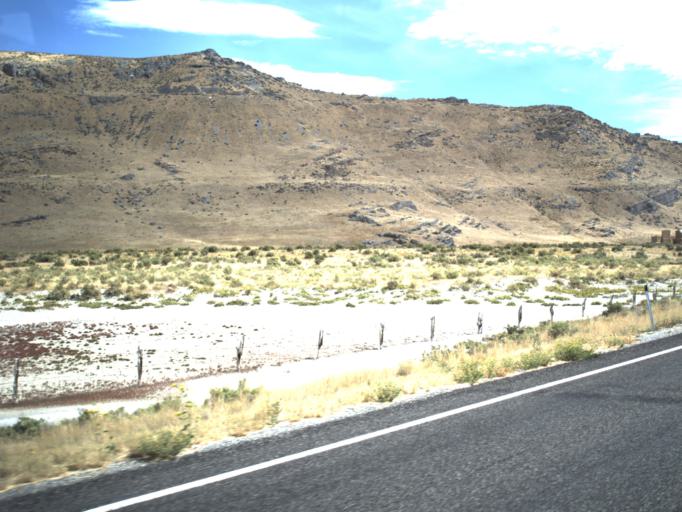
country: US
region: Utah
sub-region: Box Elder County
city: Tremonton
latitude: 41.5862
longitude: -112.2655
